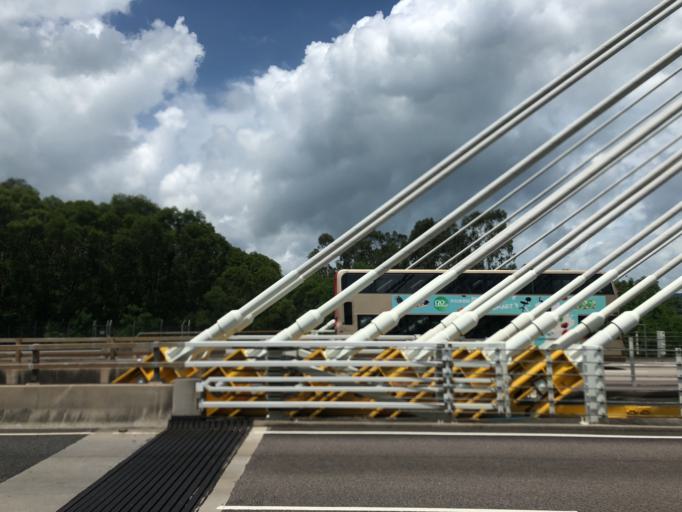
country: HK
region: Tsuen Wan
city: Tsuen Wan
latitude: 22.3595
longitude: 114.0823
